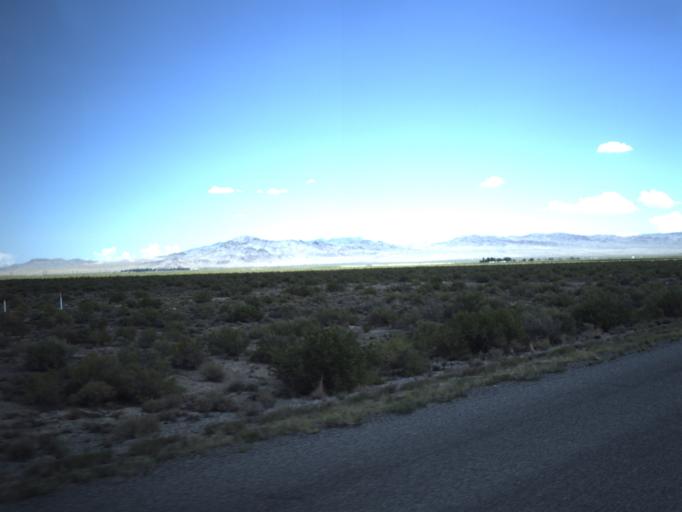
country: US
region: Nevada
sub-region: White Pine County
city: McGill
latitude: 39.0550
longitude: -114.0215
